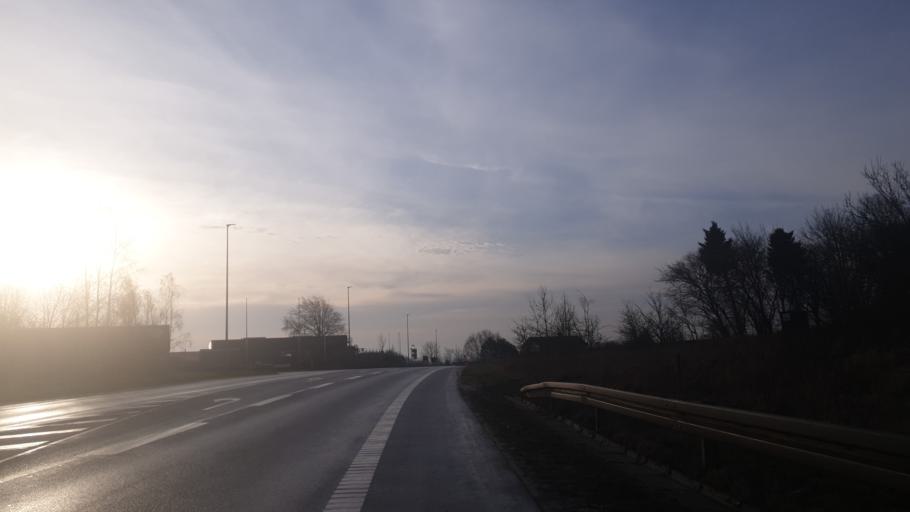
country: DK
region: Central Jutland
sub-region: Hedensted Kommune
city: Hedensted
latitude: 55.7786
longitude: 9.7099
